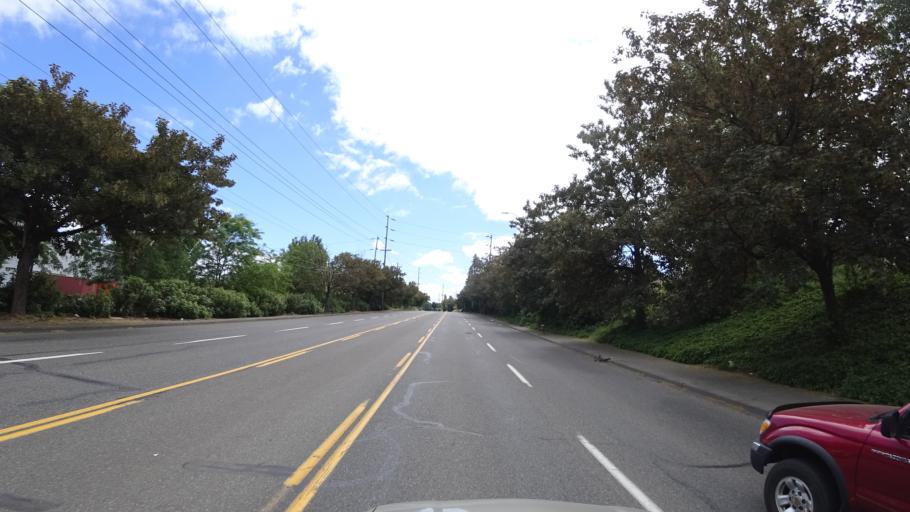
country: US
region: Oregon
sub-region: Washington County
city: West Haven
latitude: 45.6027
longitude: -122.7474
